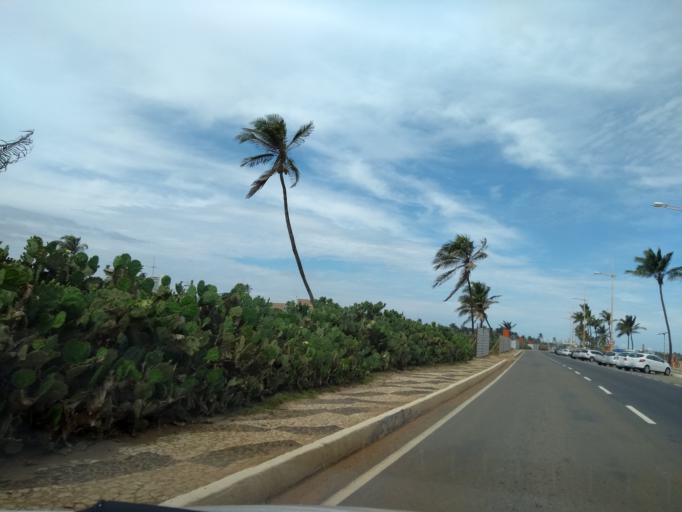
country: BR
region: Bahia
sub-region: Lauro De Freitas
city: Lauro de Freitas
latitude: -12.9586
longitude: -38.3922
